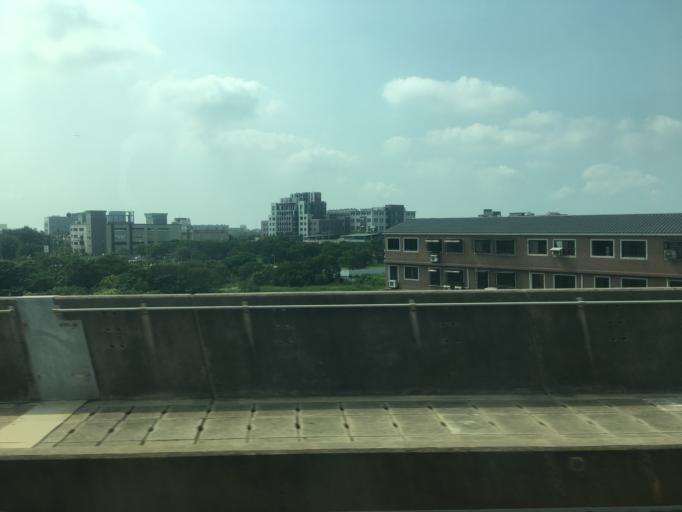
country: TW
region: Taiwan
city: Taoyuan City
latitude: 24.9604
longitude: 121.1601
